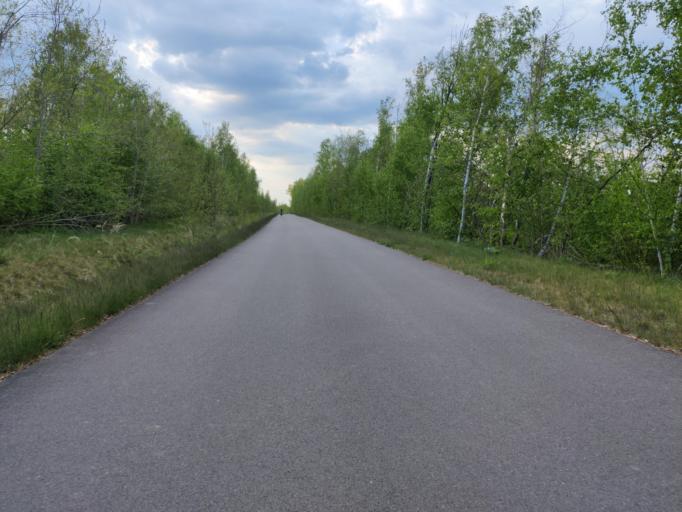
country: DE
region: Saxony
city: Espenhain
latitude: 51.2058
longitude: 12.4490
